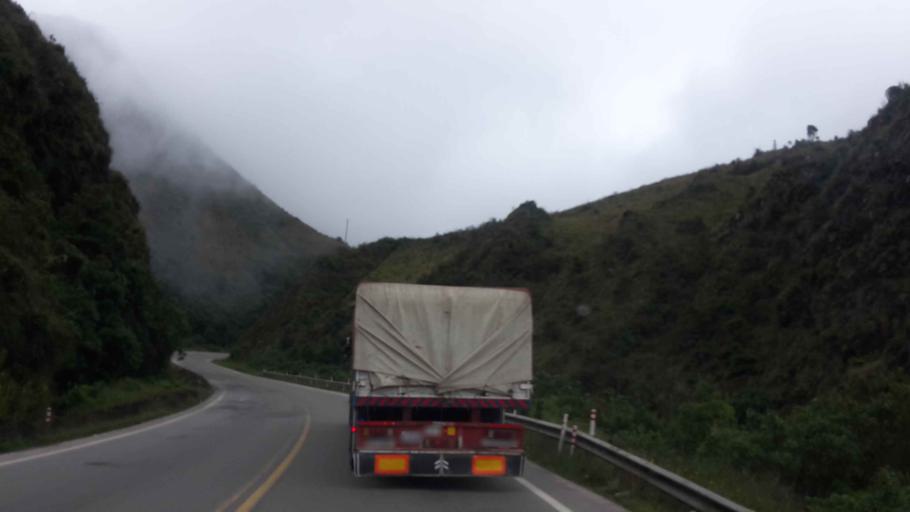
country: BO
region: Cochabamba
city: Colomi
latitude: -17.2180
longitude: -65.8924
